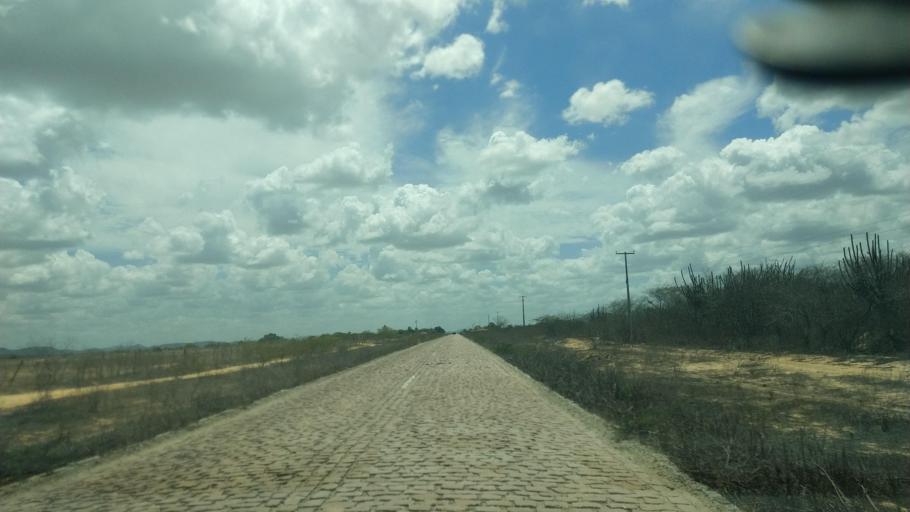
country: BR
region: Rio Grande do Norte
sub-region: Sao Paulo Do Potengi
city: Sao Paulo do Potengi
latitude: -5.9742
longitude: -35.8550
